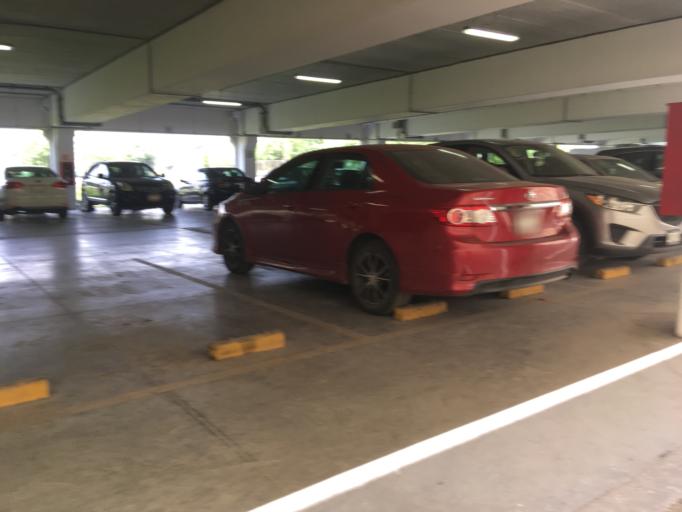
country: MX
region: Nuevo Leon
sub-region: San Nicolas de los Garza
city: San Nicolas de los Garza
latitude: 25.7264
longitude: -100.3111
